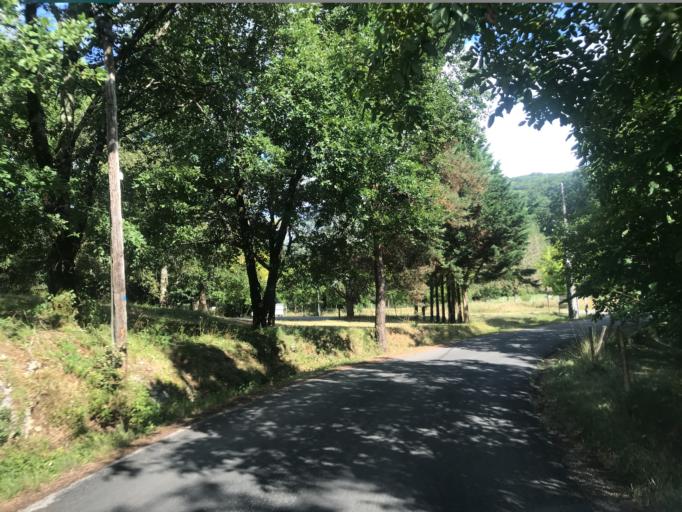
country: FR
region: Aquitaine
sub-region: Departement de la Dordogne
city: Rouffignac-Saint-Cernin-de-Reilhac
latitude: 44.9789
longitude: 1.0456
